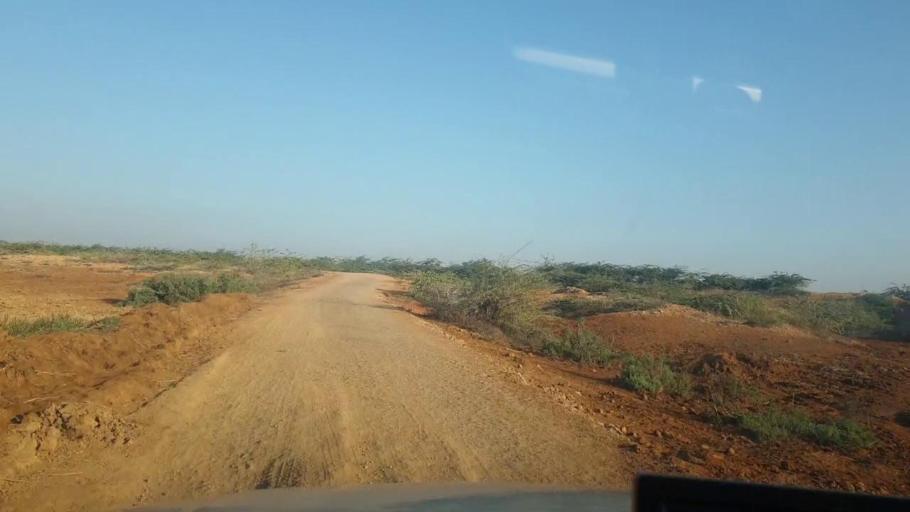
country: PK
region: Sindh
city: Thatta
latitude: 24.7058
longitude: 67.8487
